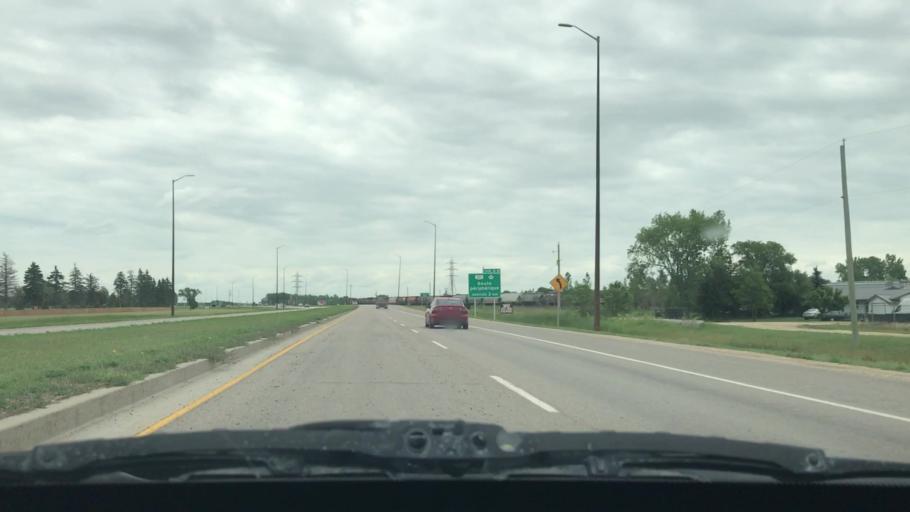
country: CA
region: Manitoba
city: Winnipeg
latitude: 49.8448
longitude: -96.9934
